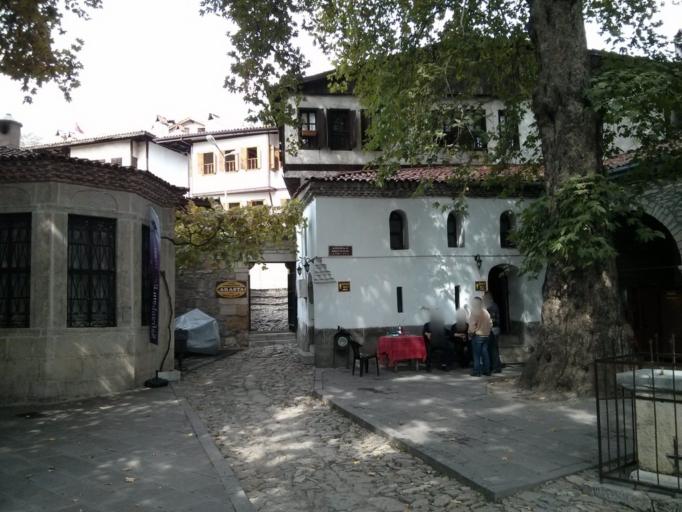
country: TR
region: Karabuk
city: Safranbolu
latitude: 41.2449
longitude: 32.6927
